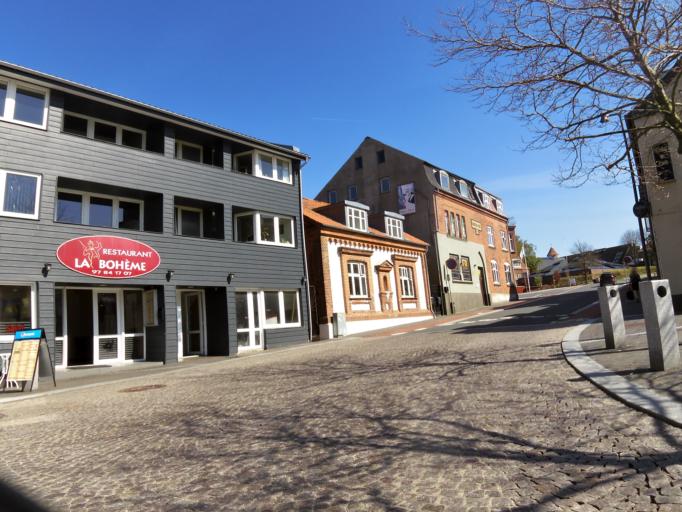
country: DK
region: Central Jutland
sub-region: Struer Kommune
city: Struer
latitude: 56.4910
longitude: 8.5981
